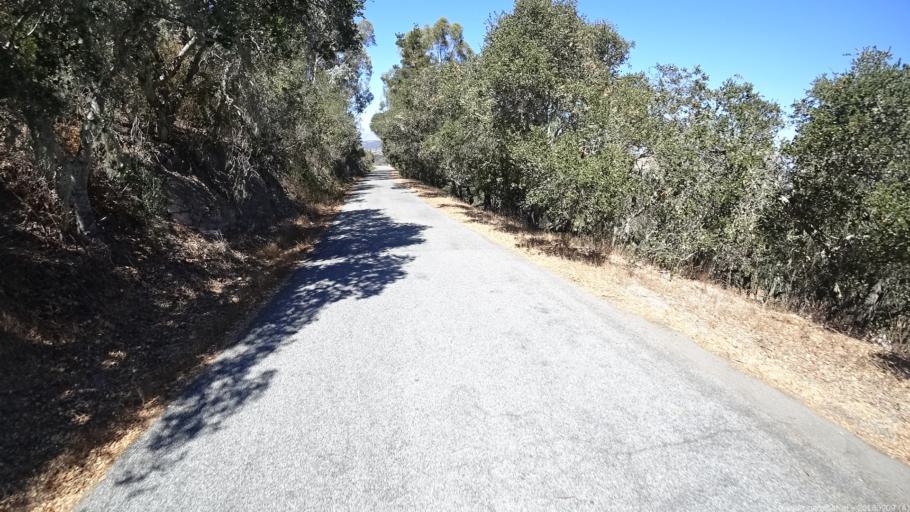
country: US
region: California
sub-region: Monterey County
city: Carmel Valley Village
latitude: 36.5500
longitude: -121.7436
